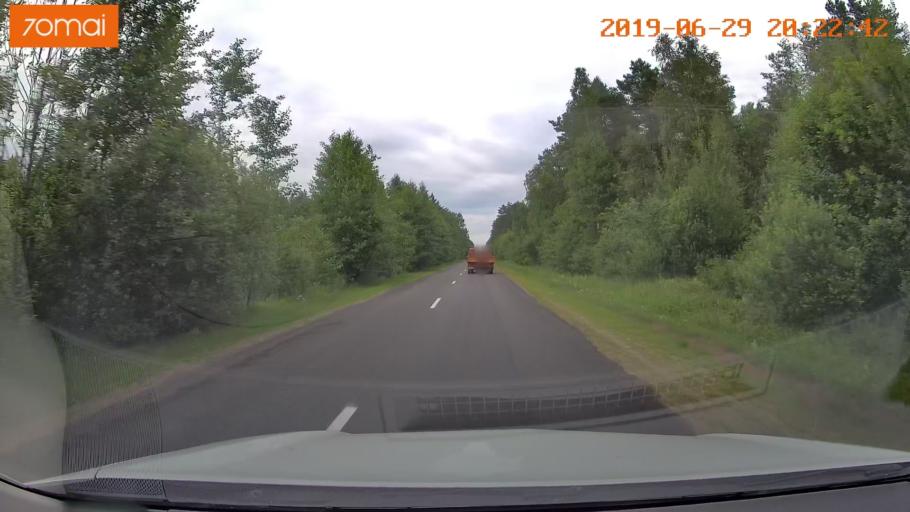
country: BY
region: Brest
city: Asnyezhytsy
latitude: 52.4355
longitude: 26.2563
